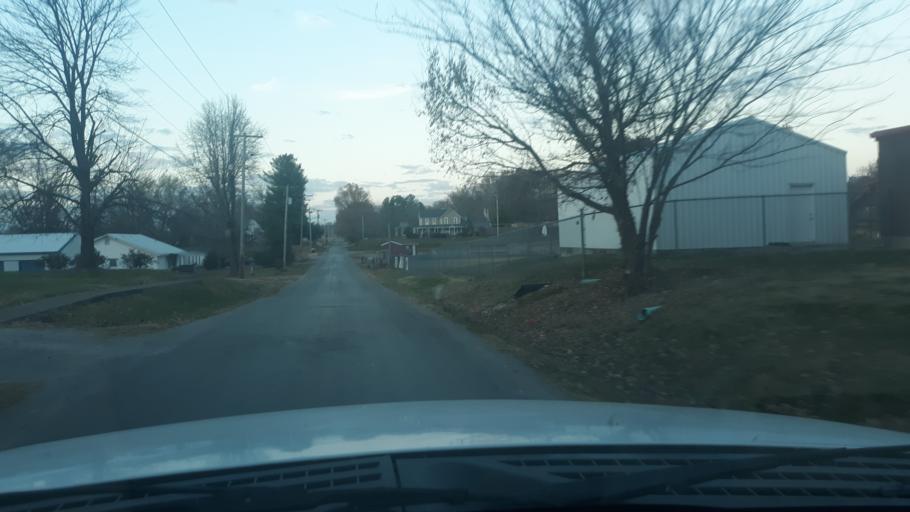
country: US
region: Illinois
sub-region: Saline County
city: Harrisburg
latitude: 37.8416
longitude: -88.6146
